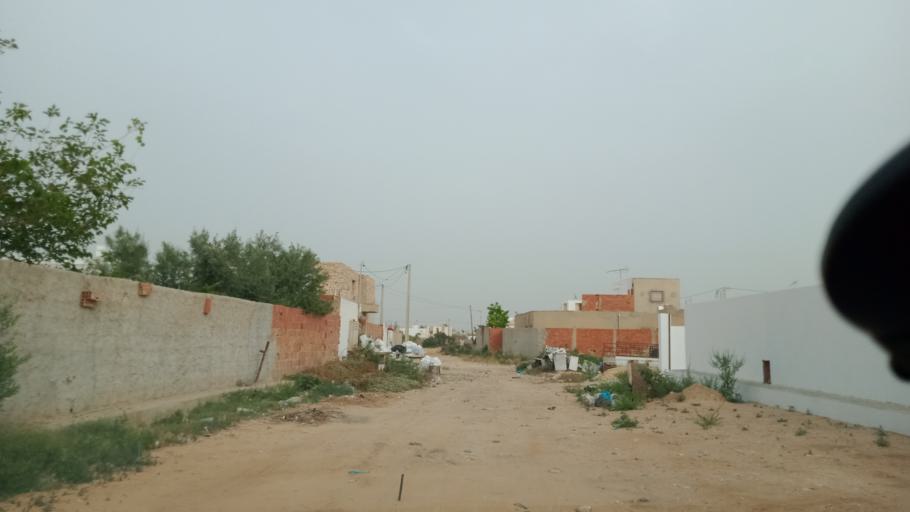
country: TN
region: Safaqis
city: Al Qarmadah
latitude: 34.7947
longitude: 10.7663
